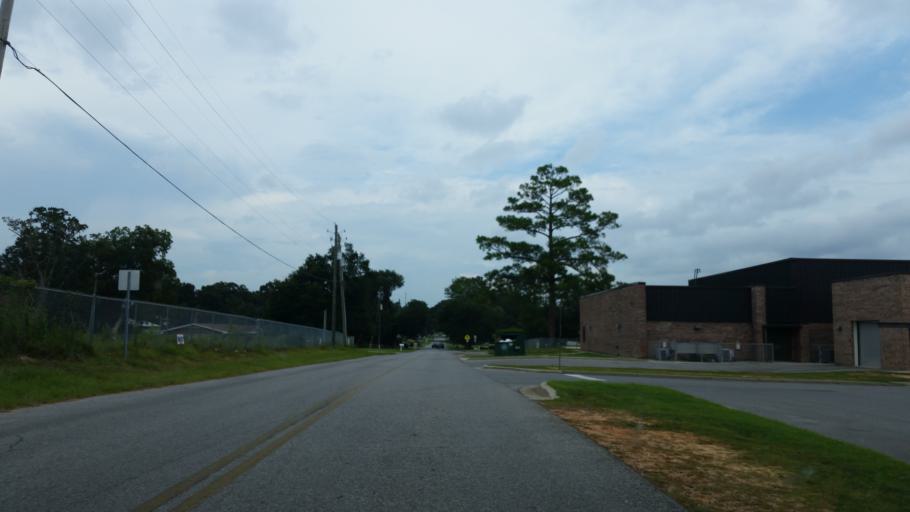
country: US
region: Florida
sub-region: Santa Rosa County
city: Pace
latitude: 30.6039
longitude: -87.1545
